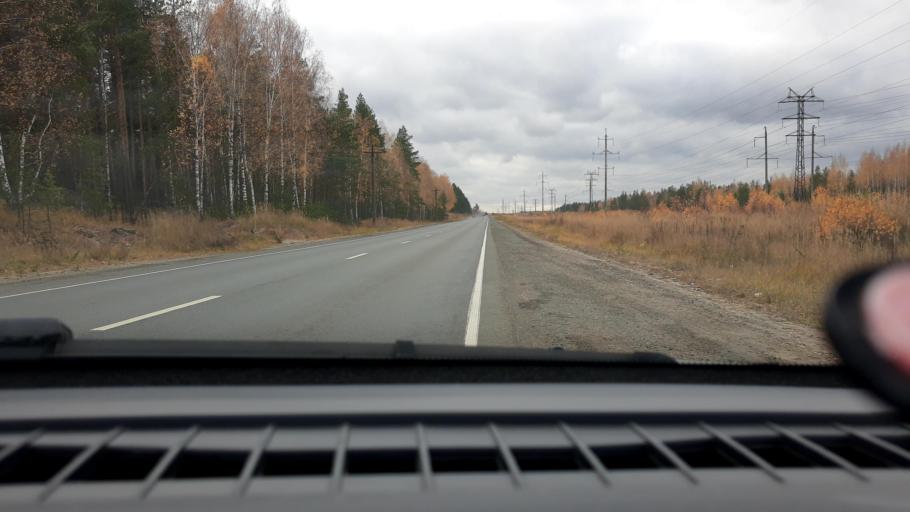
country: RU
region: Nizjnij Novgorod
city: Lukino
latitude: 56.3512
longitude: 43.5882
